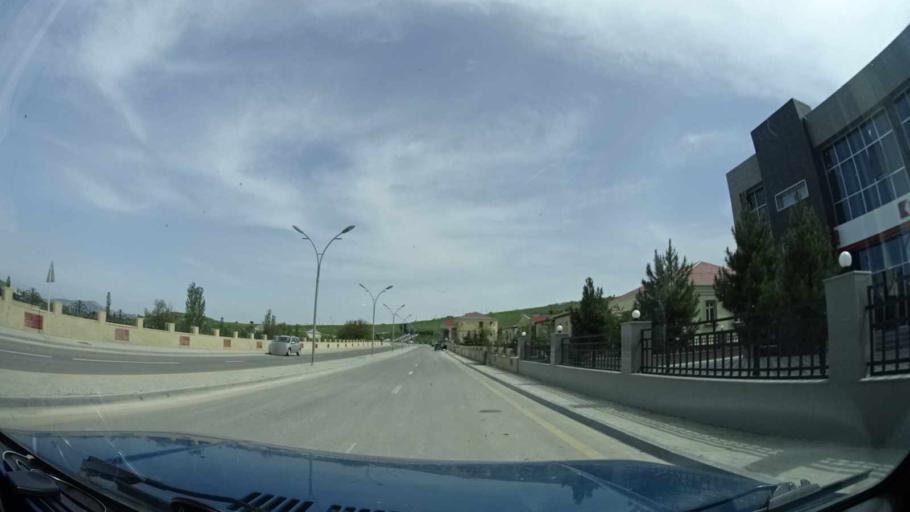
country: AZ
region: Xizi
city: Khyzy
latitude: 40.9110
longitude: 49.0740
